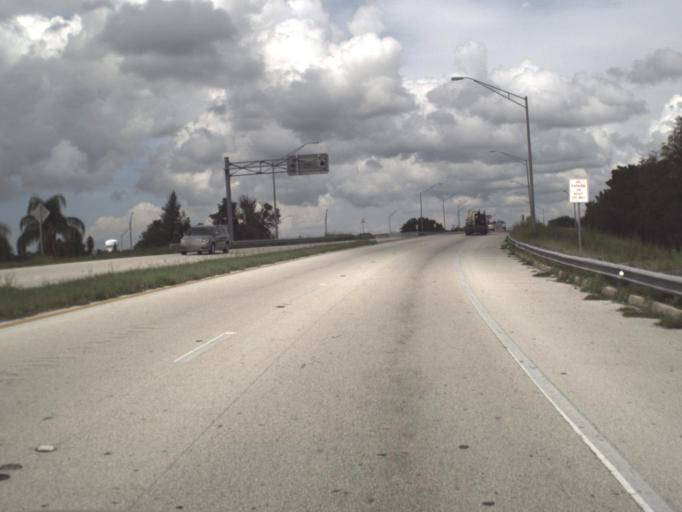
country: US
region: Florida
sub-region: Manatee County
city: Palmetto
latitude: 27.5196
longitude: -82.5629
